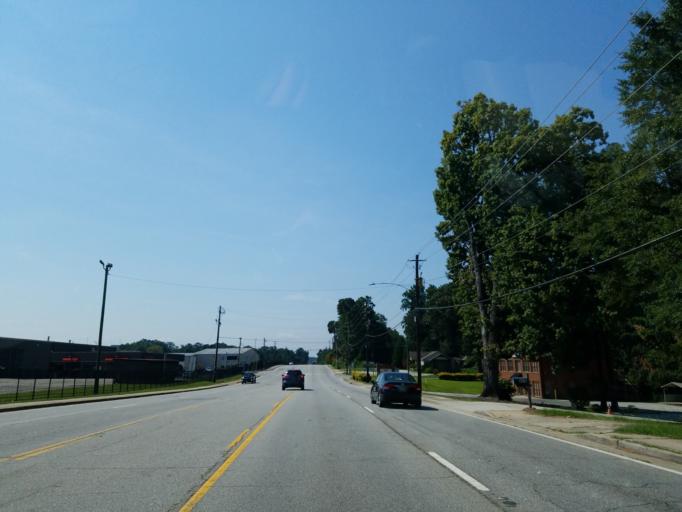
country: US
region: Georgia
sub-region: DeKalb County
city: Chamblee
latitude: 33.8778
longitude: -84.3095
